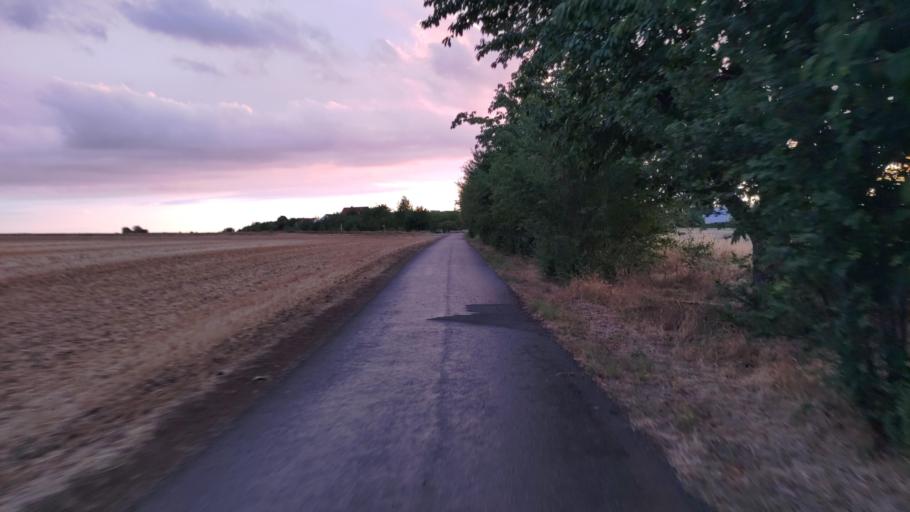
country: DE
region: Thuringia
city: Erfurt
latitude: 50.9884
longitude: 11.0795
